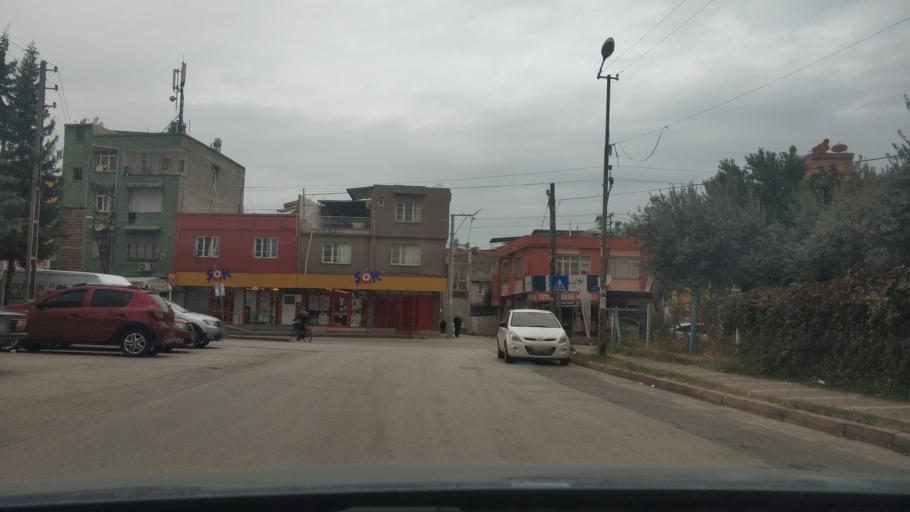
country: TR
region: Adana
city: Yuregir
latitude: 37.0051
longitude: 35.3604
